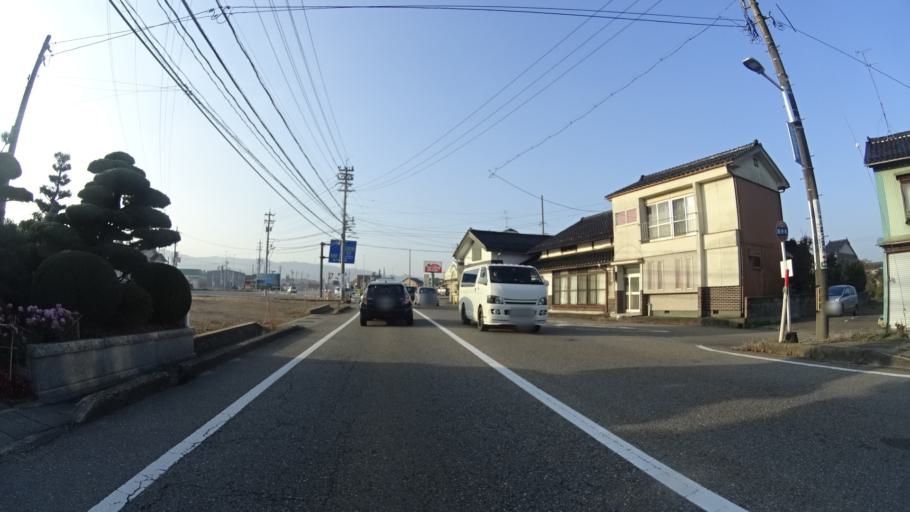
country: JP
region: Ishikawa
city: Nanao
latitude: 37.0330
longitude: 136.9677
